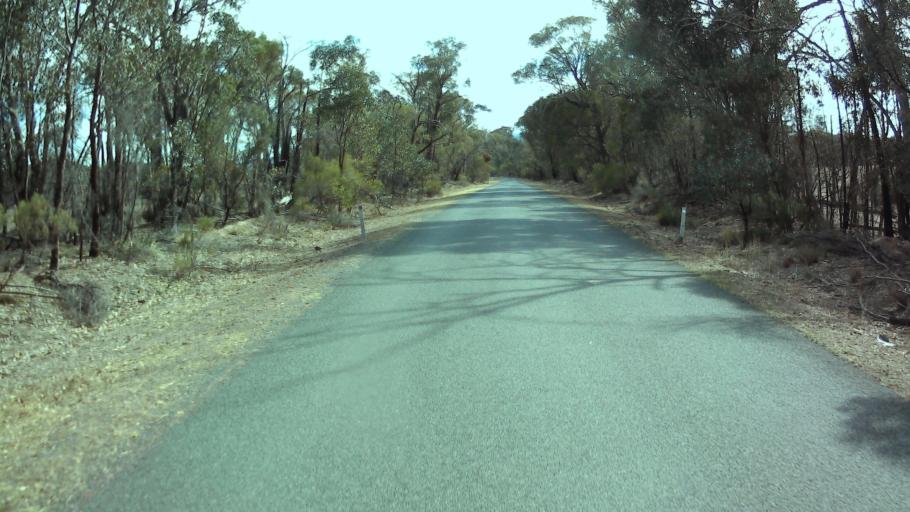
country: AU
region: New South Wales
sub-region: Weddin
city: Grenfell
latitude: -33.8714
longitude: 148.2028
